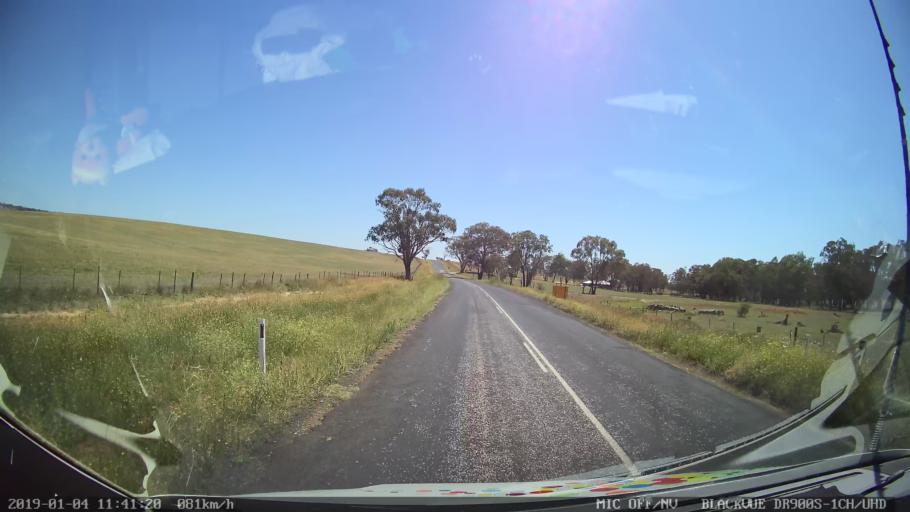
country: AU
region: New South Wales
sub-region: Cabonne
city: Molong
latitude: -32.9949
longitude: 148.7874
